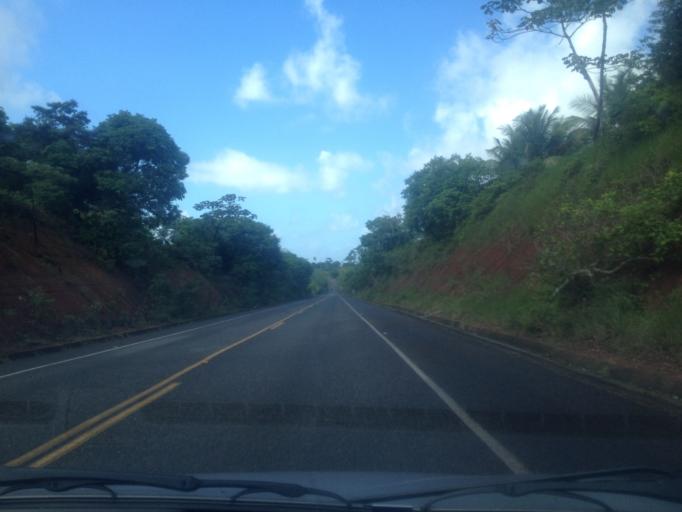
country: BR
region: Bahia
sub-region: Conde
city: Conde
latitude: -12.0552
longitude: -37.7309
